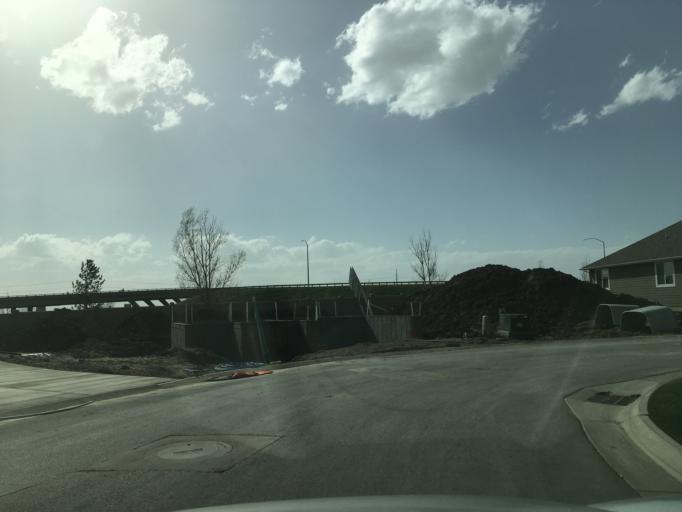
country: US
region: Utah
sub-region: Davis County
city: Farmington
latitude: 40.9708
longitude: -111.8904
